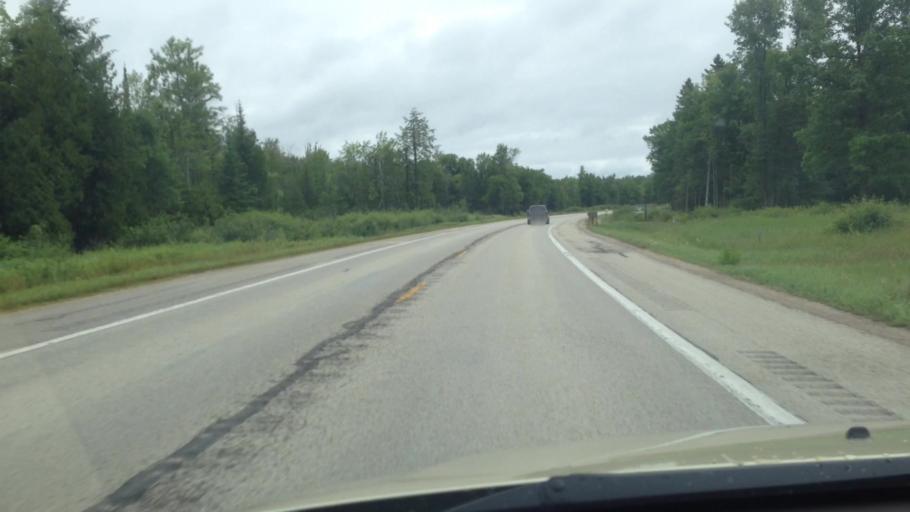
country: US
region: Michigan
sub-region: Delta County
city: Escanaba
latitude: 45.6617
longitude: -87.1737
